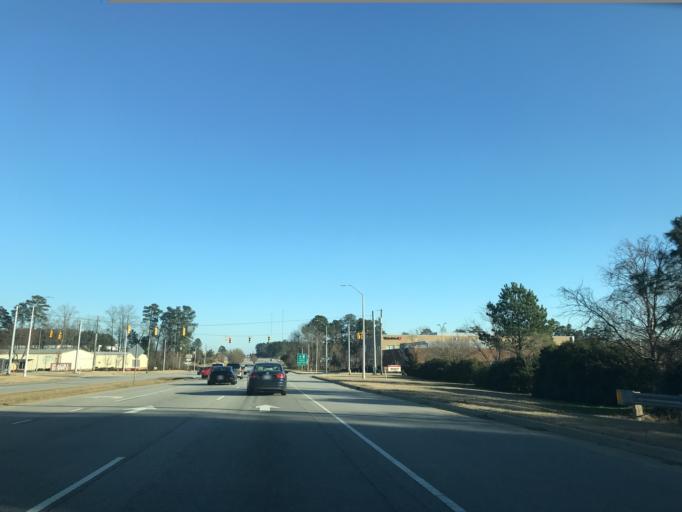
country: US
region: North Carolina
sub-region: Wake County
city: Garner
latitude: 35.7004
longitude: -78.5973
